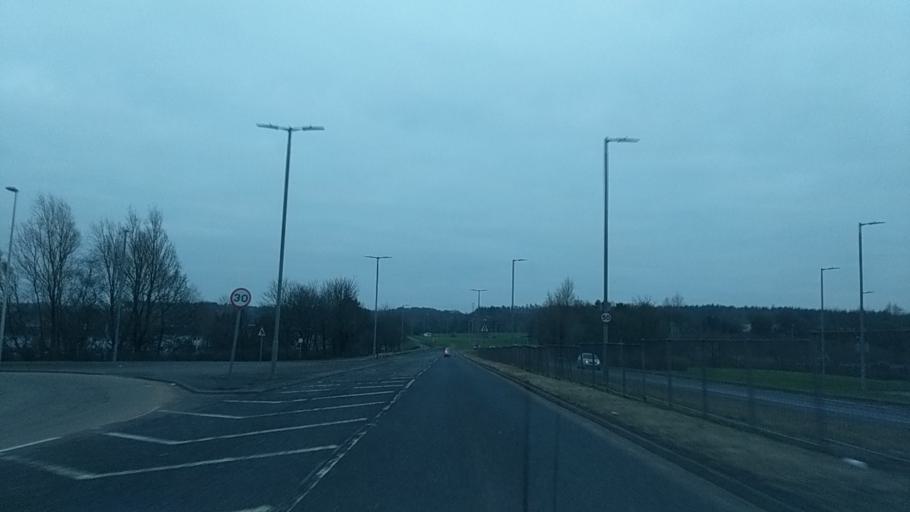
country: GB
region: Scotland
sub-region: South Lanarkshire
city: East Kilbride
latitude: 55.7541
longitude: -4.1573
